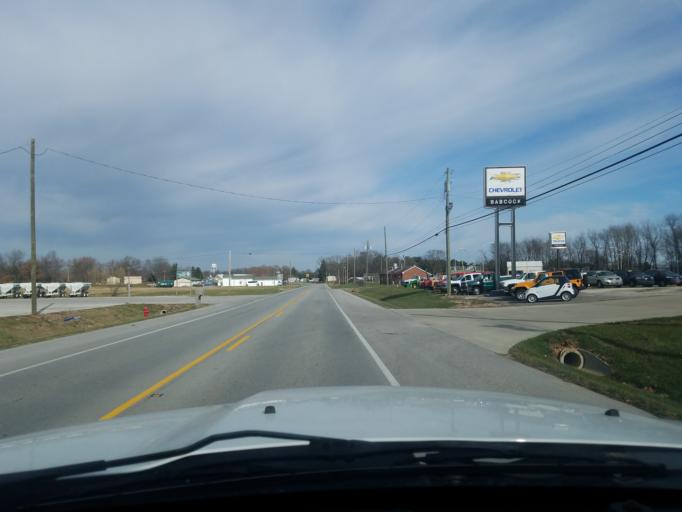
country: US
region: Indiana
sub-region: Orange County
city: Orleans
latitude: 38.6507
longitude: -86.4550
